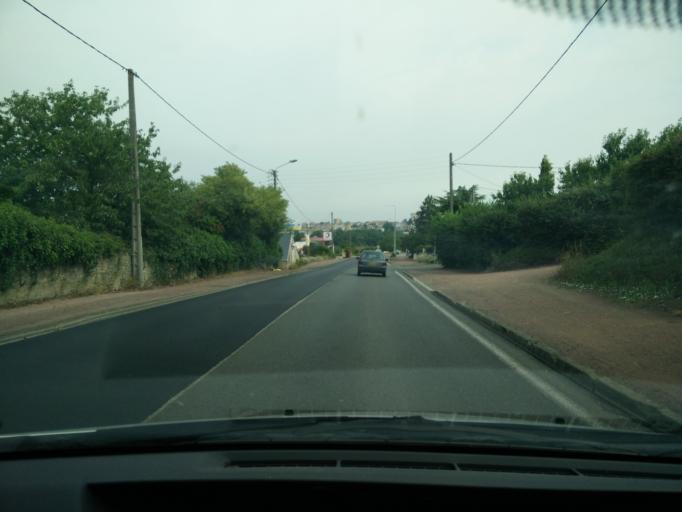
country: FR
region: Poitou-Charentes
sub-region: Departement des Deux-Sevres
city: Saint-Jean-de-Thouars
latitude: 46.9659
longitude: -0.2106
